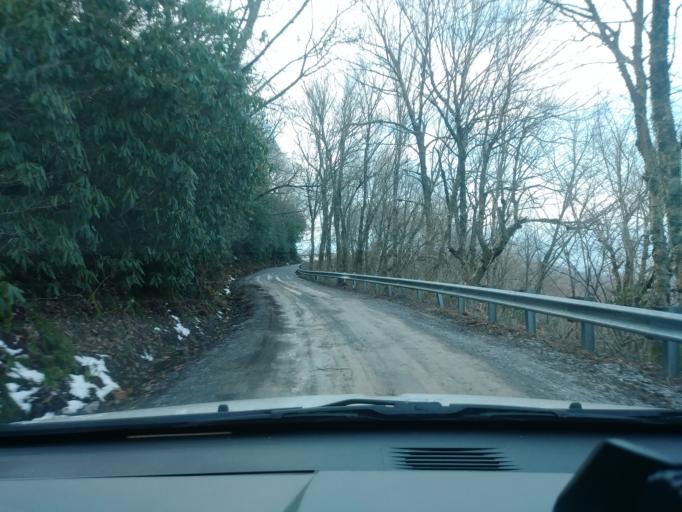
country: US
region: Tennessee
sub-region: Greene County
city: Tusculum
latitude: 36.0310
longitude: -82.7122
